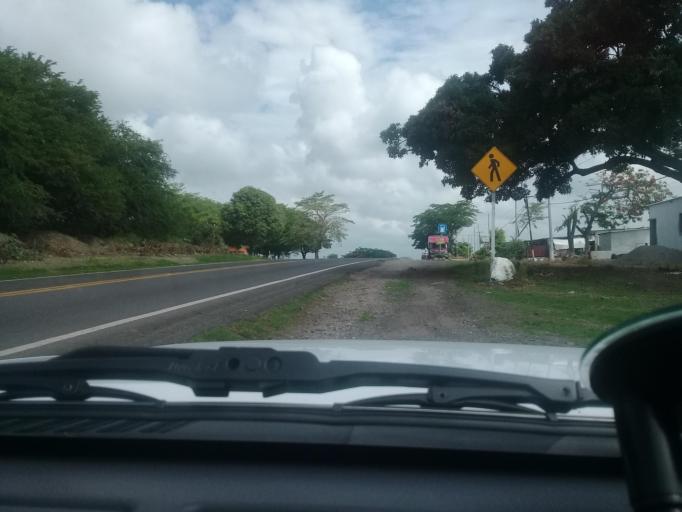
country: MX
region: Veracruz
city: Paso de Ovejas
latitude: 19.2736
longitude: -96.4207
